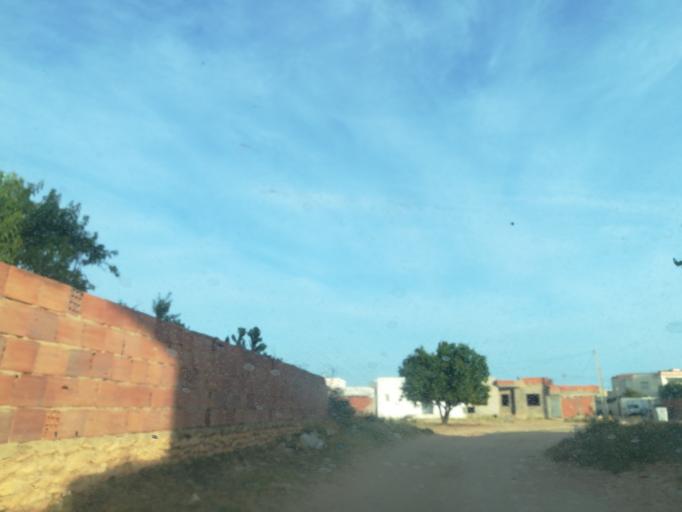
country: TN
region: Safaqis
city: Al Qarmadah
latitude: 34.8135
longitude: 10.7534
